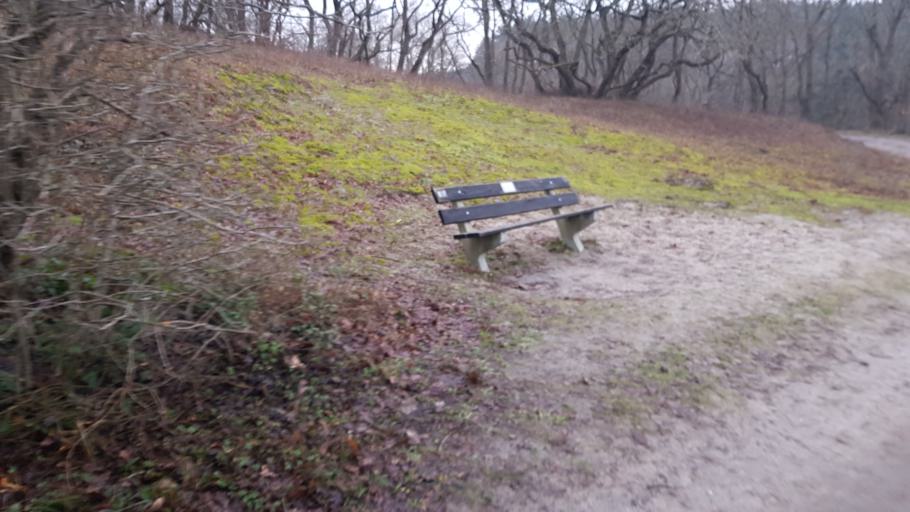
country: NL
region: North Holland
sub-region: Gemeente Bergen
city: Egmond aan Zee
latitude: 52.6476
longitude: 4.6551
